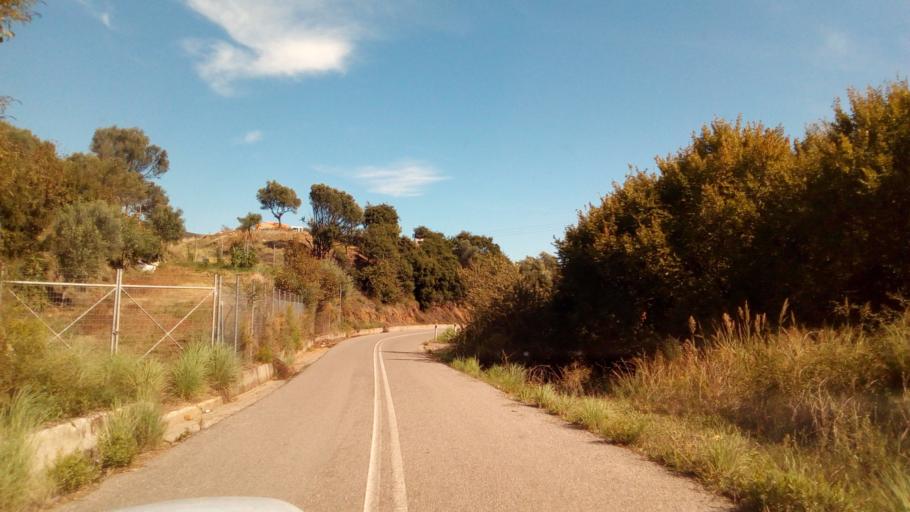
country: GR
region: West Greece
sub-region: Nomos Aitolias kai Akarnanias
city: Antirrio
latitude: 38.3685
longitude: 21.7700
